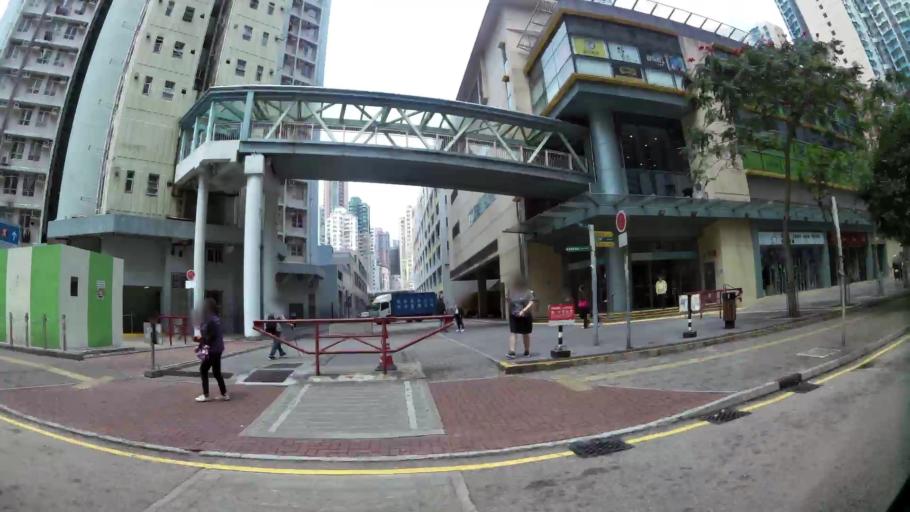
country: HK
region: Wanchai
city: Wan Chai
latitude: 22.2804
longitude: 114.2281
